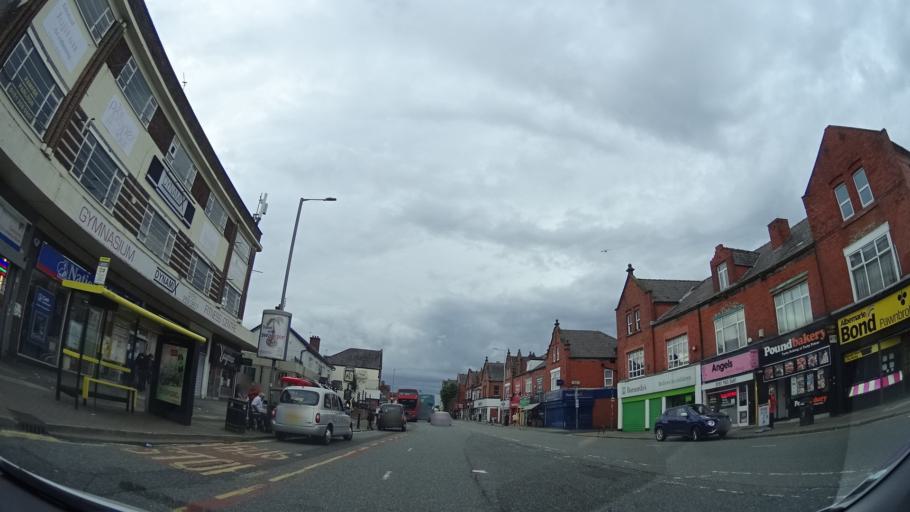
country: GB
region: England
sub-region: Liverpool
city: Liverpool
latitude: 53.4139
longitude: -2.9103
